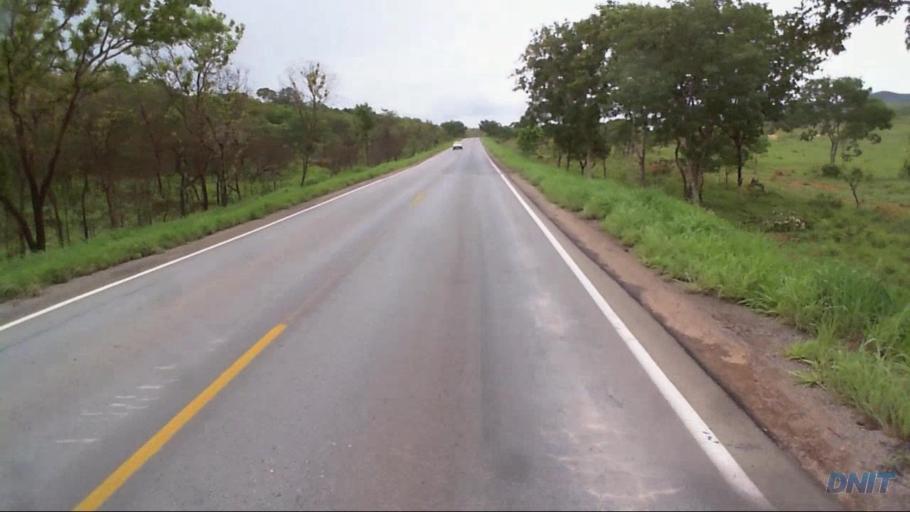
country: BR
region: Goias
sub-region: Padre Bernardo
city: Padre Bernardo
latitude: -15.4528
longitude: -48.2108
